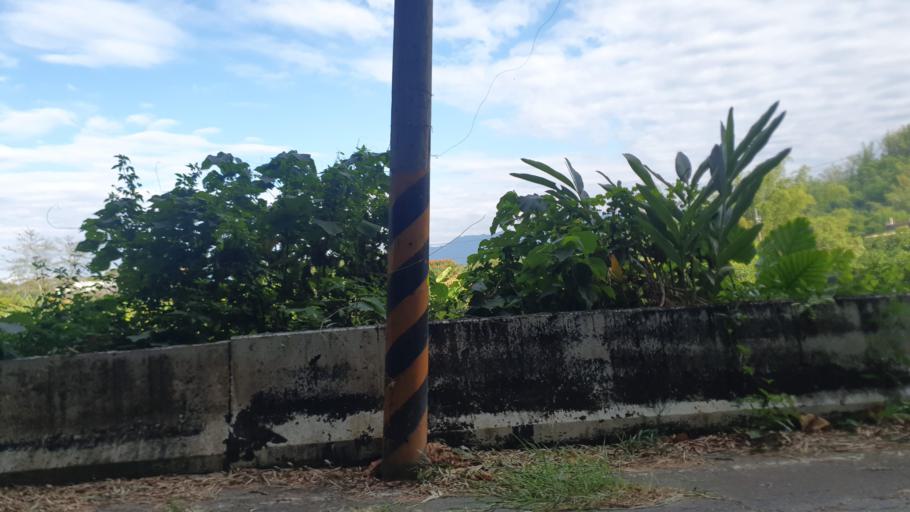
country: TW
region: Taiwan
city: Yujing
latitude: 23.0270
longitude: 120.4123
